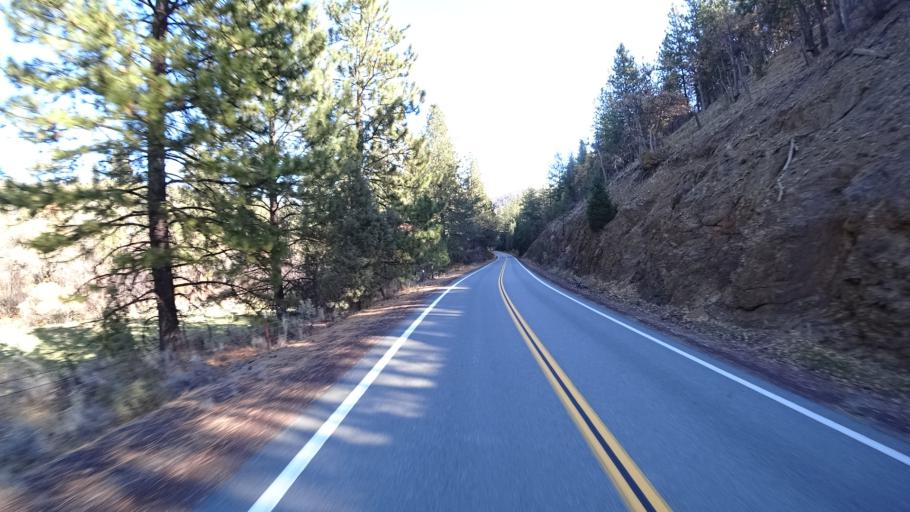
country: US
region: California
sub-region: Siskiyou County
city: Weed
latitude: 41.4658
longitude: -122.6060
